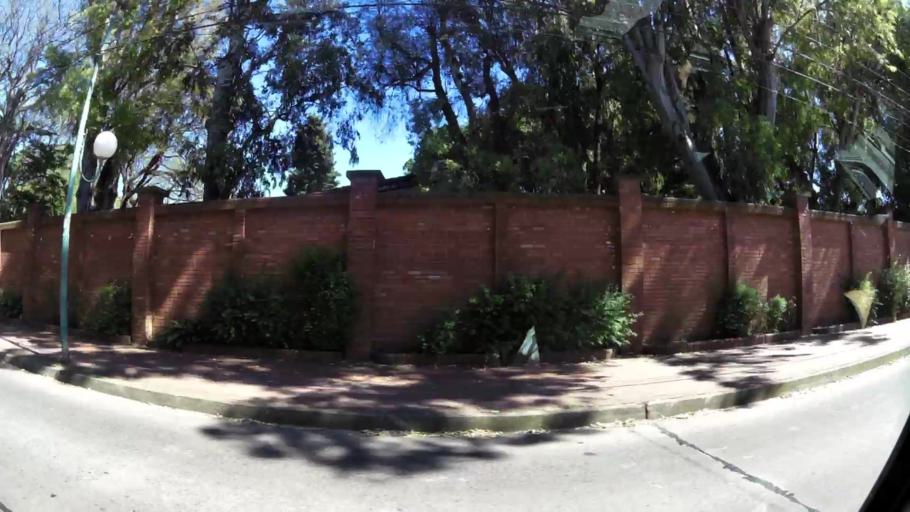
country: AR
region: Buenos Aires
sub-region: Partido de Vicente Lopez
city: Olivos
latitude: -34.5158
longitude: -58.4815
